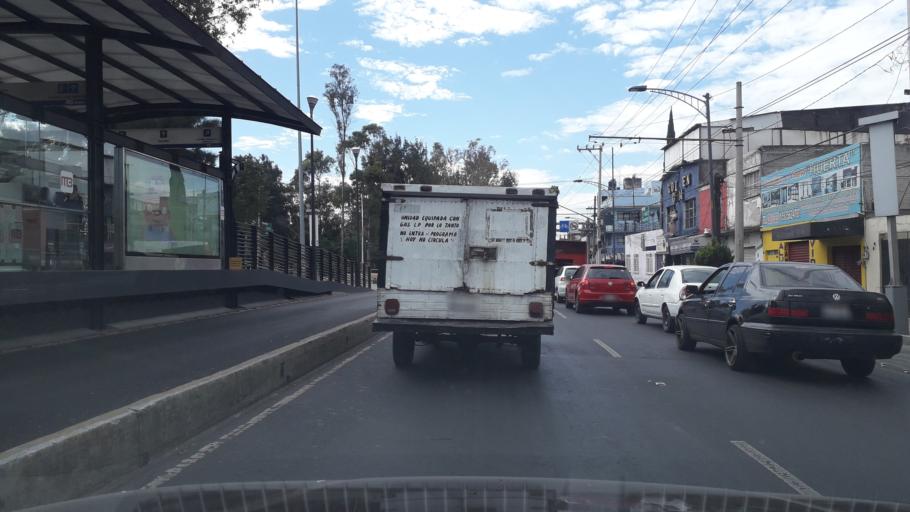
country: MX
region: Mexico City
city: Gustavo A. Madero
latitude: 19.4674
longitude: -99.1030
